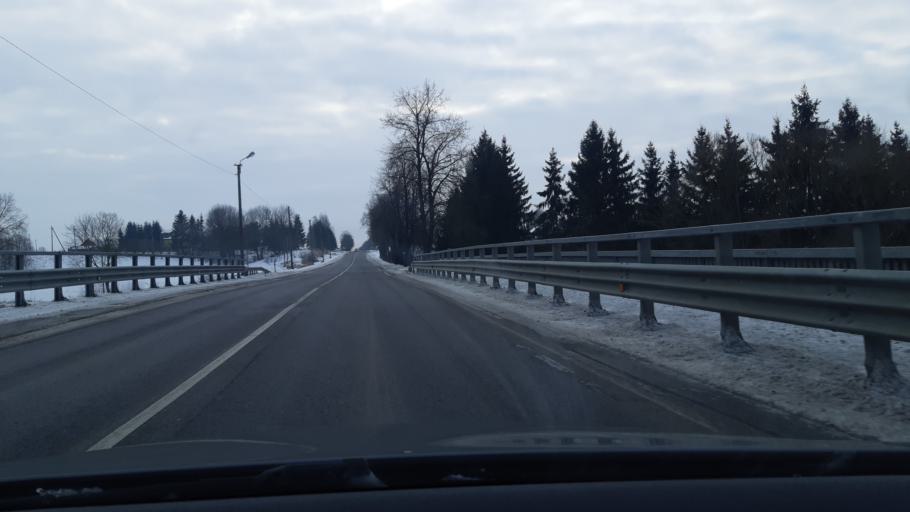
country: LT
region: Kauno apskritis
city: Kedainiai
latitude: 55.2425
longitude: 23.8330
